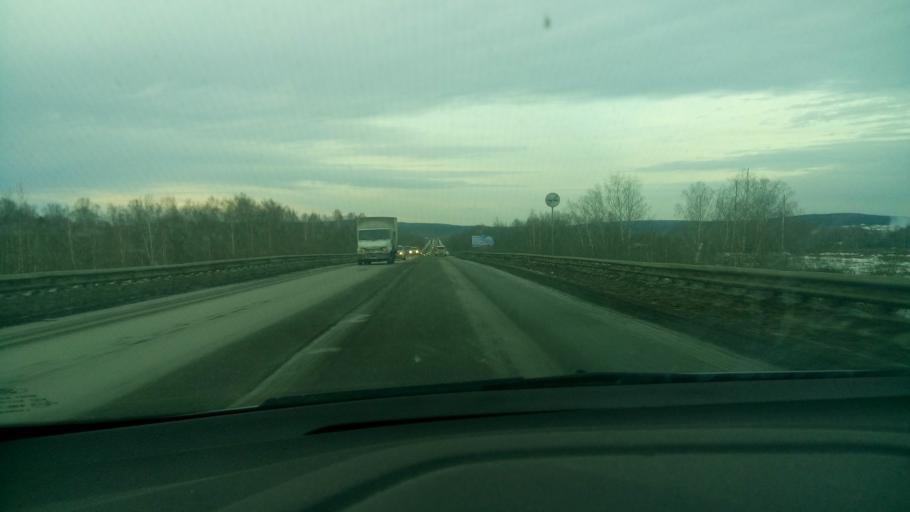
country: RU
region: Sverdlovsk
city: Istok
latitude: 56.7511
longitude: 60.7531
